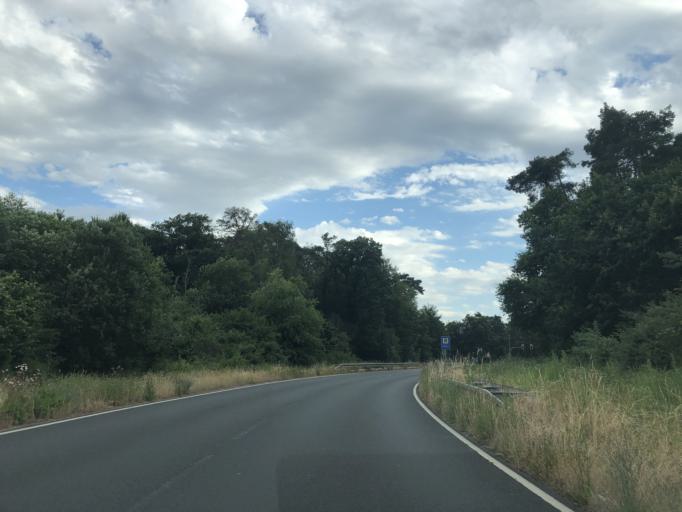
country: DE
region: Hesse
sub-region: Regierungsbezirk Darmstadt
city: Dietzenbach
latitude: 50.0144
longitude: 8.8057
